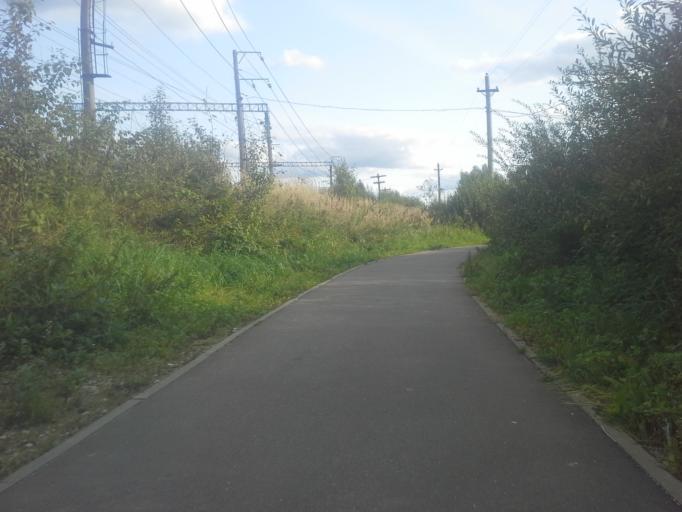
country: RU
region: Moskovskaya
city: Kievskij
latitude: 55.4225
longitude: 36.8676
